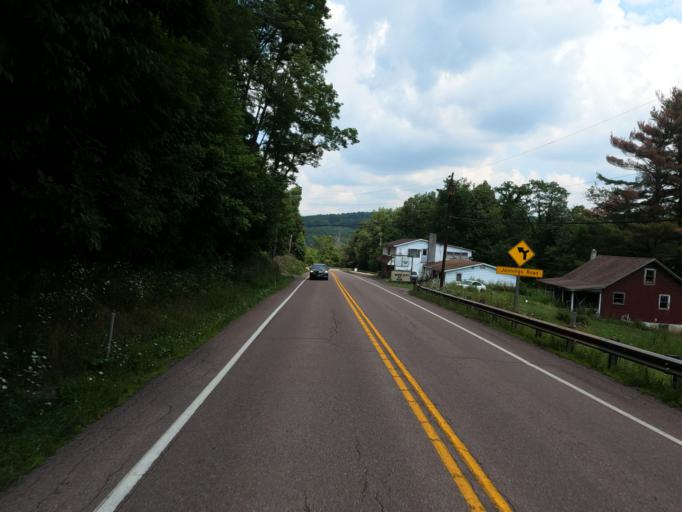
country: US
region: Maryland
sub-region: Allegany County
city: Westernport
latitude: 39.6549
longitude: -79.1848
